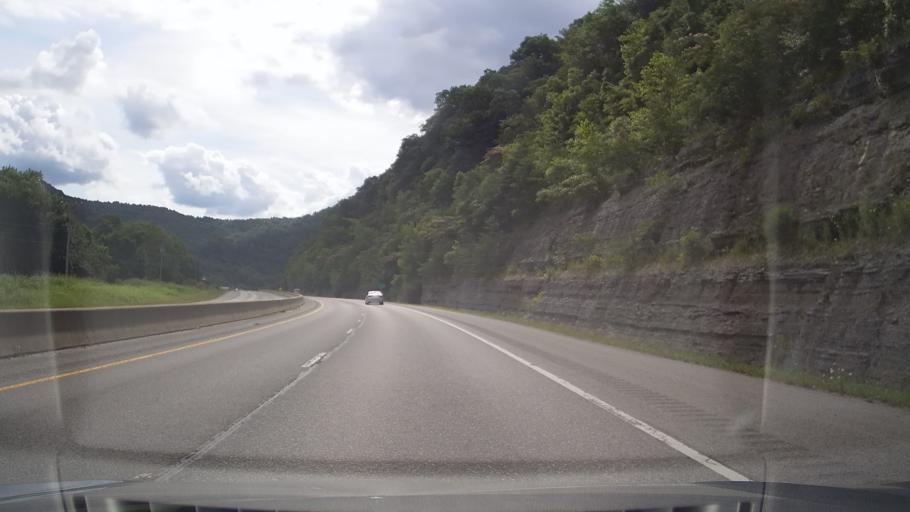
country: US
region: Kentucky
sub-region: Pike County
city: Coal Run Village
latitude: 37.5752
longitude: -82.6487
